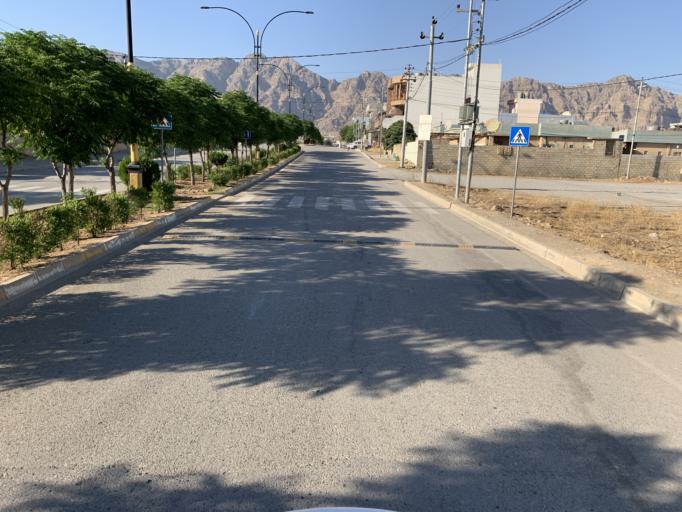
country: IQ
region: As Sulaymaniyah
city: Raniye
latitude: 36.2440
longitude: 44.8733
